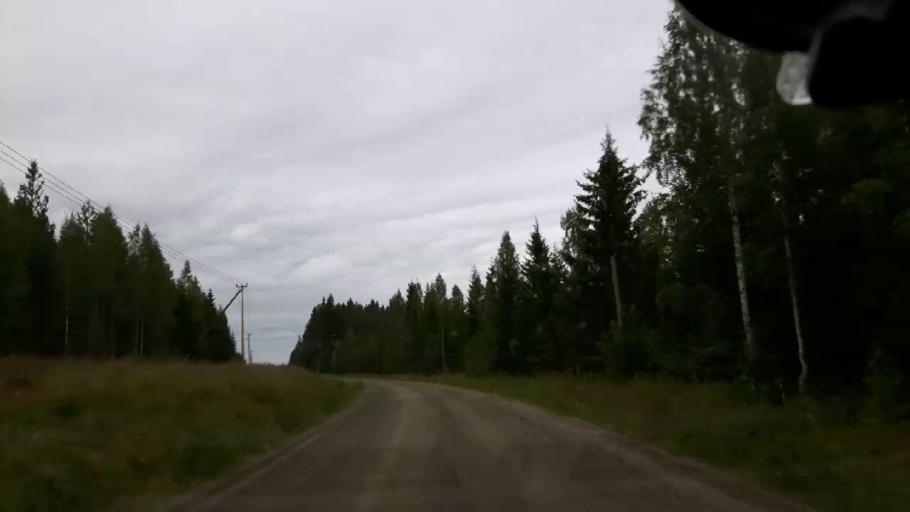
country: SE
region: Jaemtland
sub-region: Braecke Kommun
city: Braecke
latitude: 63.0252
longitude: 15.3723
